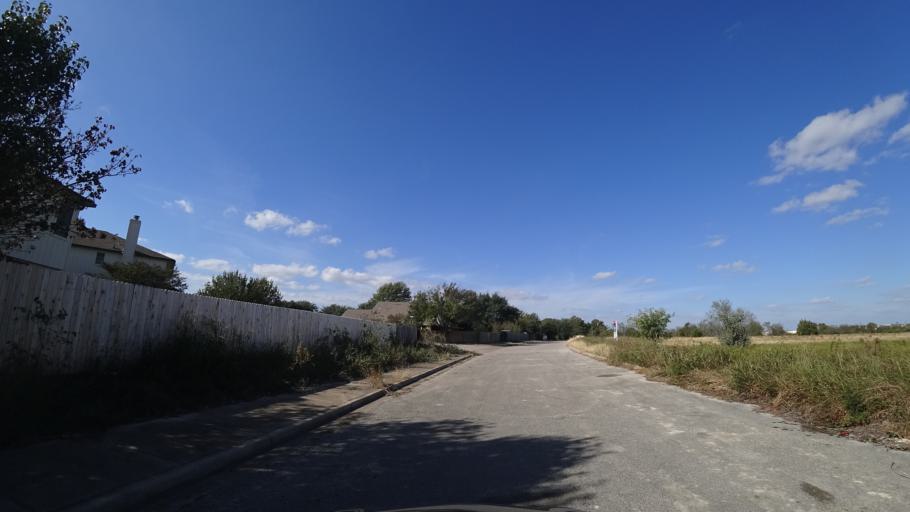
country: US
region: Texas
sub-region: Travis County
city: Wells Branch
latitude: 30.4596
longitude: -97.6799
